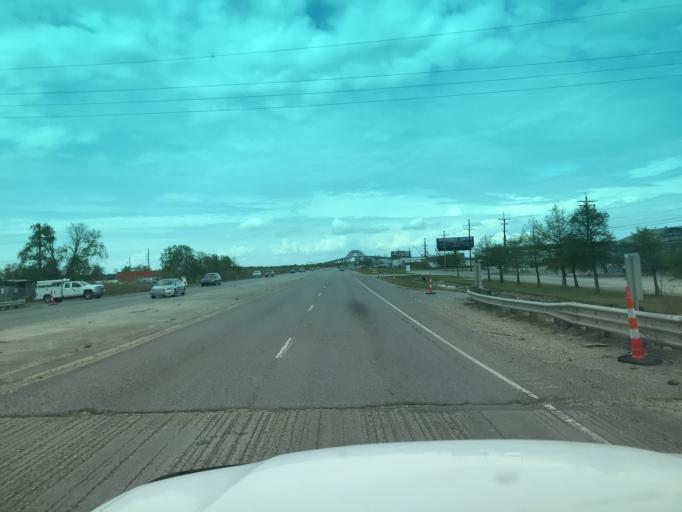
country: US
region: Louisiana
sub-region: Saint Bernard Parish
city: Chalmette
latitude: 29.9822
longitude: -89.9452
